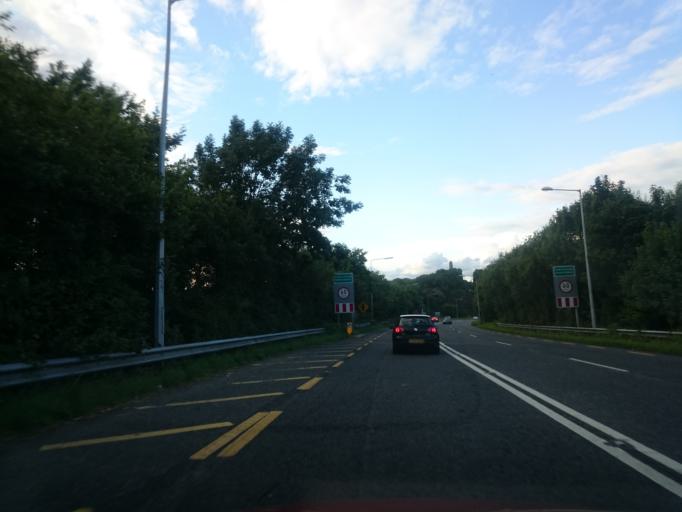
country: IE
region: Leinster
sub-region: Loch Garman
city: Loch Garman
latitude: 52.3468
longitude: -6.5146
